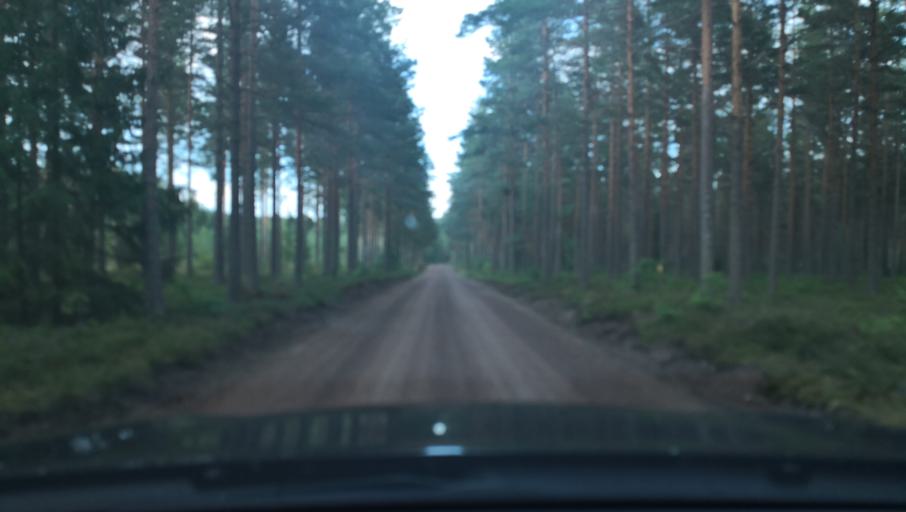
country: SE
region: Kalmar
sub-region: Hultsfreds Kommun
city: Malilla
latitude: 57.3925
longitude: 15.7552
